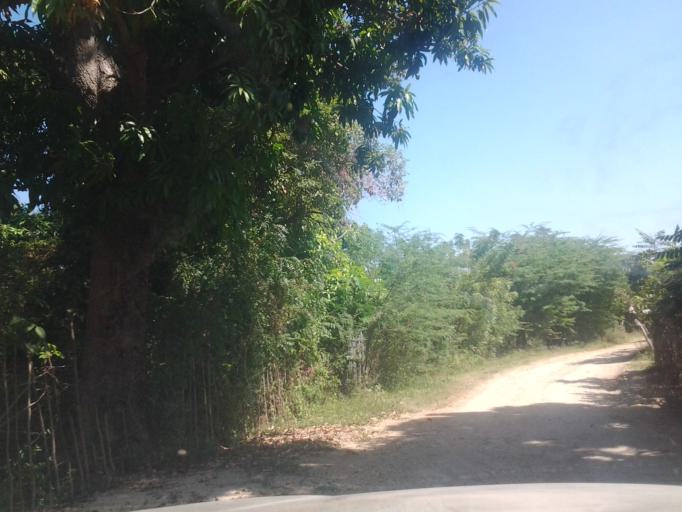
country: HT
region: Ouest
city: Grangwav
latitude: 18.4283
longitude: -72.7917
